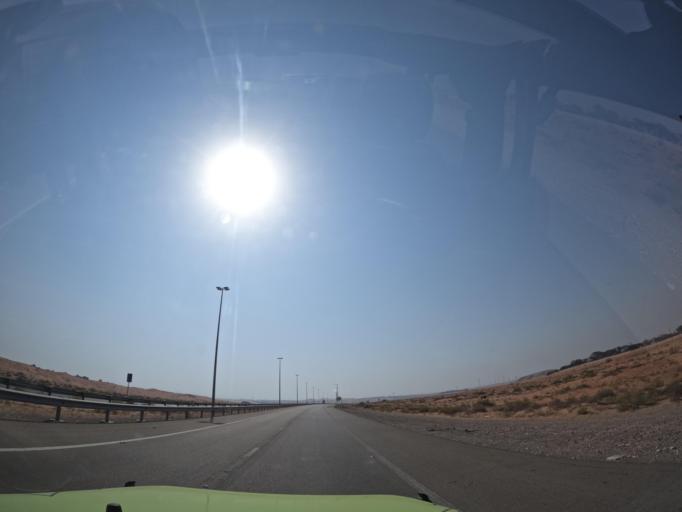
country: OM
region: Al Buraimi
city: Al Buraymi
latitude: 24.3989
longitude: 55.7162
